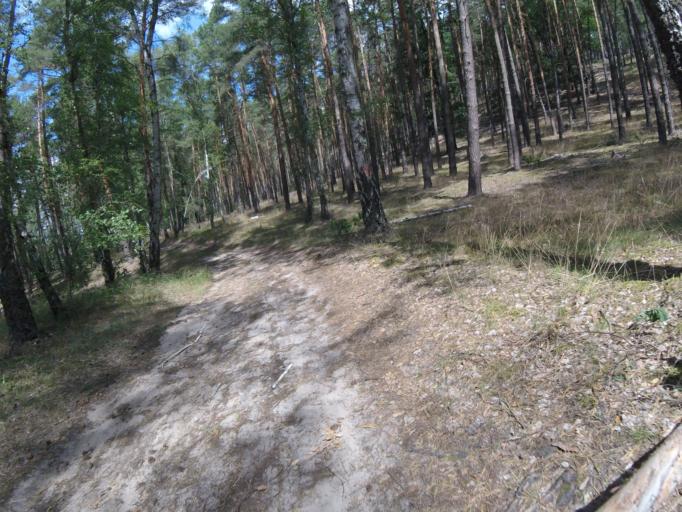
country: DE
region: Brandenburg
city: Bestensee
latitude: 52.2066
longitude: 13.6391
